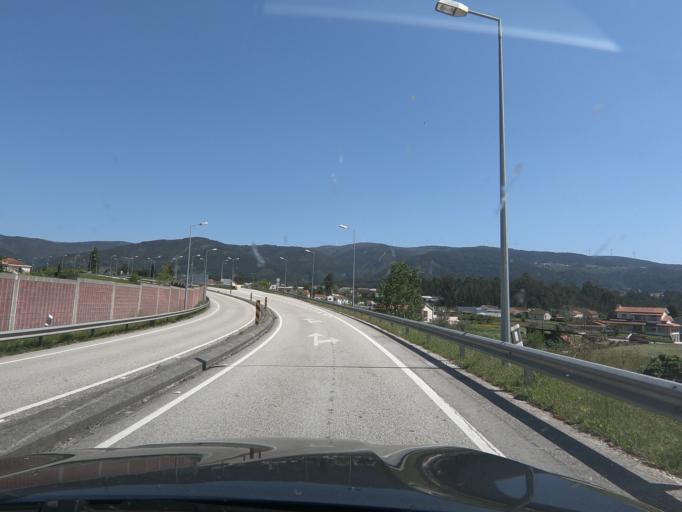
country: PT
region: Coimbra
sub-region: Miranda do Corvo
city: Miranda do Corvo
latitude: 40.0840
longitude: -8.3309
